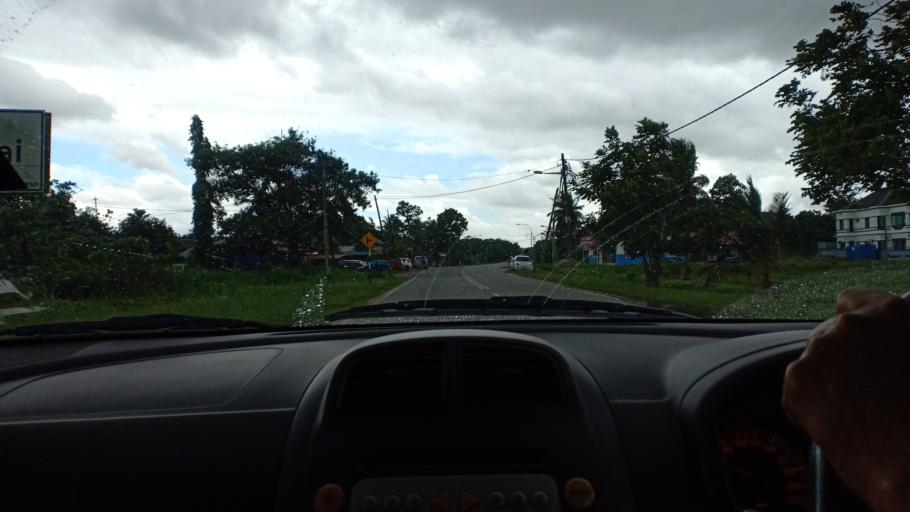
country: MY
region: Penang
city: Tasek Glugor
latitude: 5.4427
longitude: 100.4731
